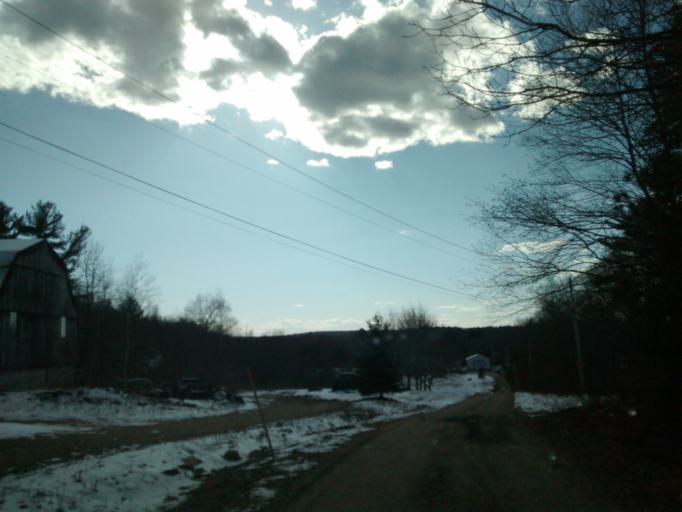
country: US
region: Massachusetts
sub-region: Worcester County
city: Uxbridge
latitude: 42.0298
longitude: -71.6566
